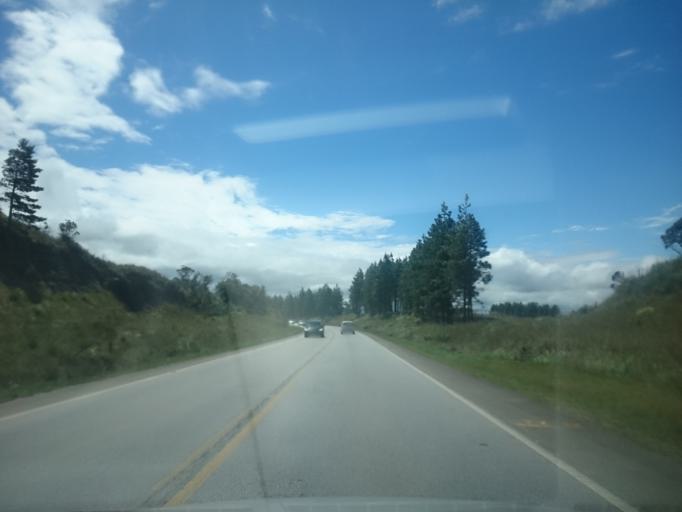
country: BR
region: Santa Catarina
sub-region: Anitapolis
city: Anitapolis
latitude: -27.6829
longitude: -49.1438
